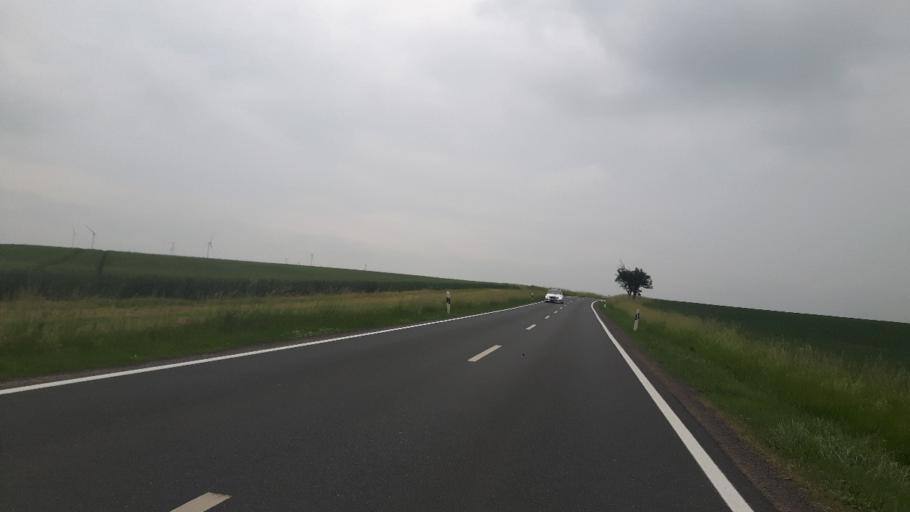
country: DE
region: Bavaria
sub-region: Regierungsbezirk Unterfranken
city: Schwanfeld
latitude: 49.9023
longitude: 10.1259
